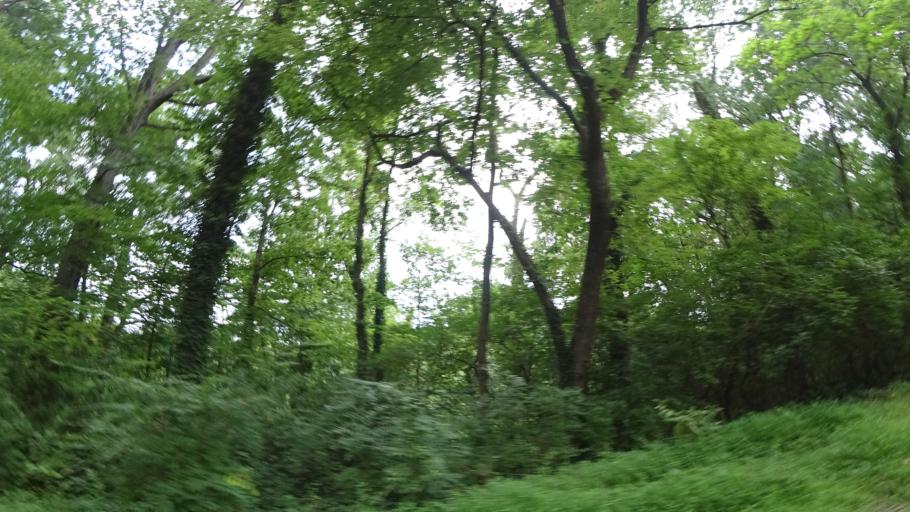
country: US
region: Maryland
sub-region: Prince George's County
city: Colmar Manor
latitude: 38.9110
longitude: -76.9643
